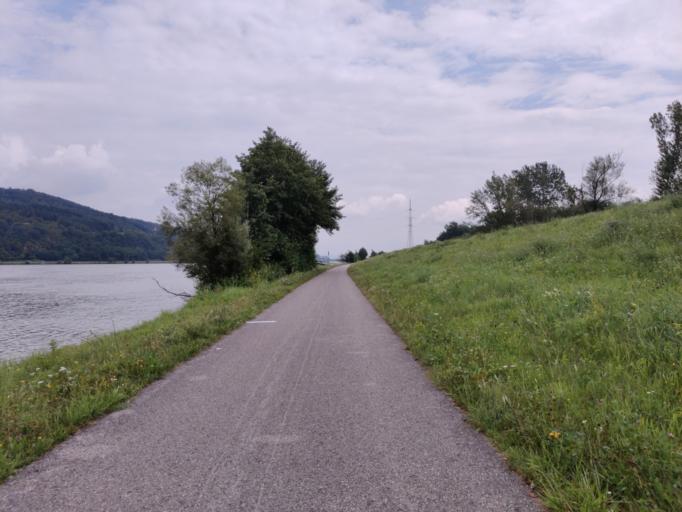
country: AT
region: Lower Austria
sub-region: Politischer Bezirk Melk
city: Pochlarn
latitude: 48.2140
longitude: 15.1771
